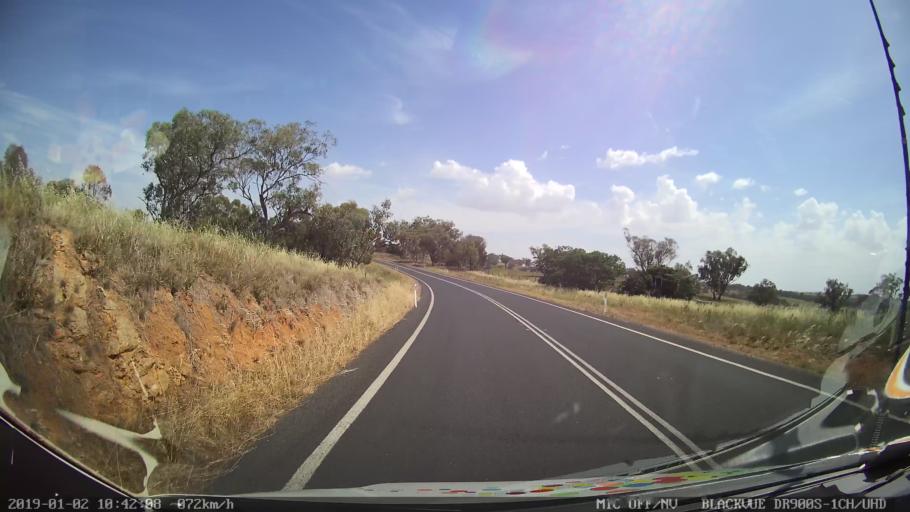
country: AU
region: New South Wales
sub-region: Cootamundra
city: Cootamundra
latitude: -34.7879
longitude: 148.3086
